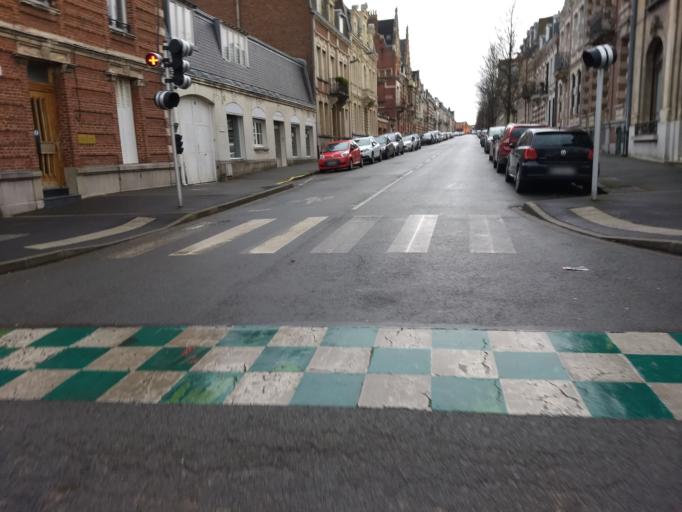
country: FR
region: Nord-Pas-de-Calais
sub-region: Departement du Pas-de-Calais
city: Arras
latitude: 50.2873
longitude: 2.7714
